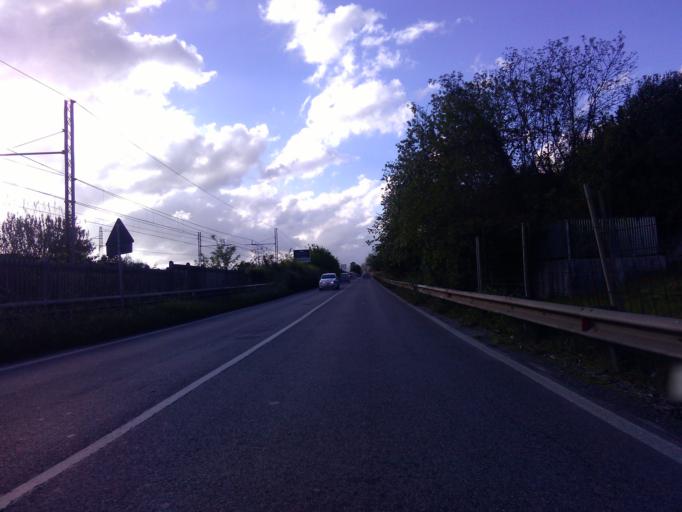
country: IT
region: Tuscany
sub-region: Provincia di Massa-Carrara
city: Capanne-Prato-Cinquale
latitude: 44.0015
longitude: 10.1670
